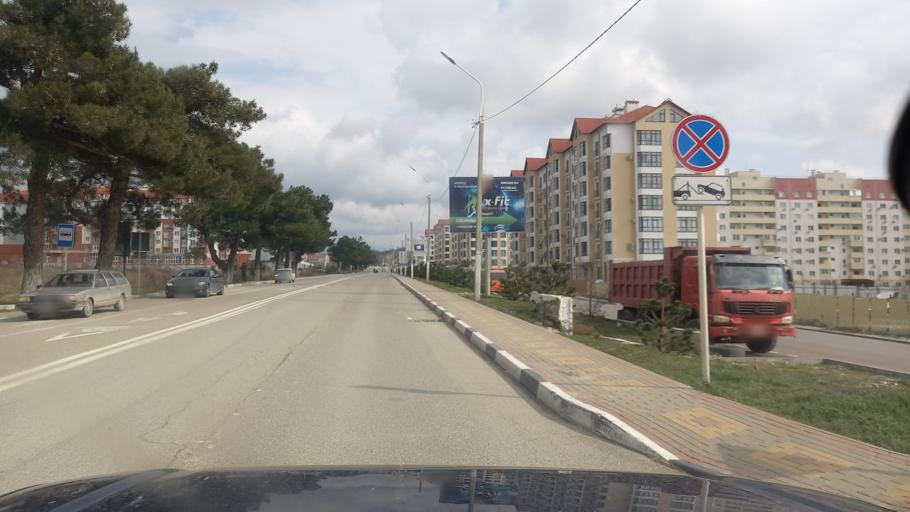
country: RU
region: Krasnodarskiy
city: Gelendzhik
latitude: 44.5579
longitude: 38.1015
